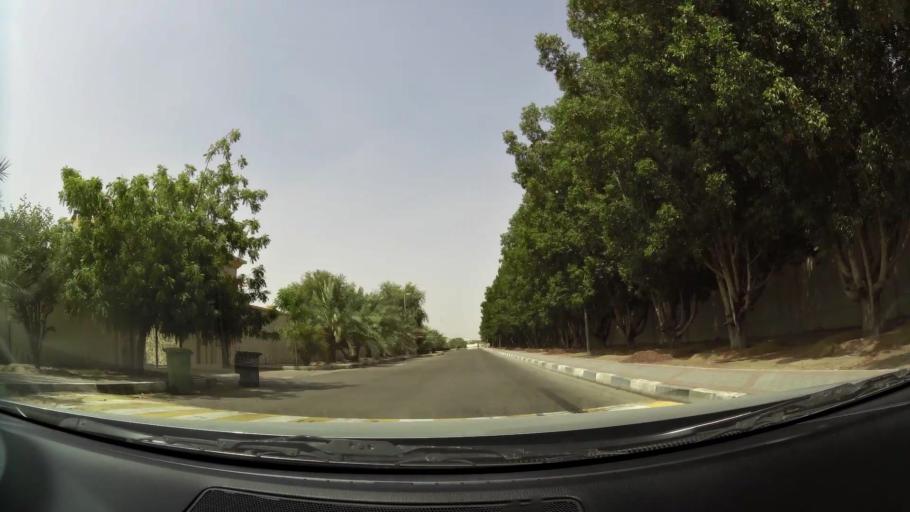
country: AE
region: Abu Dhabi
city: Al Ain
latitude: 24.1578
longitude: 55.6581
